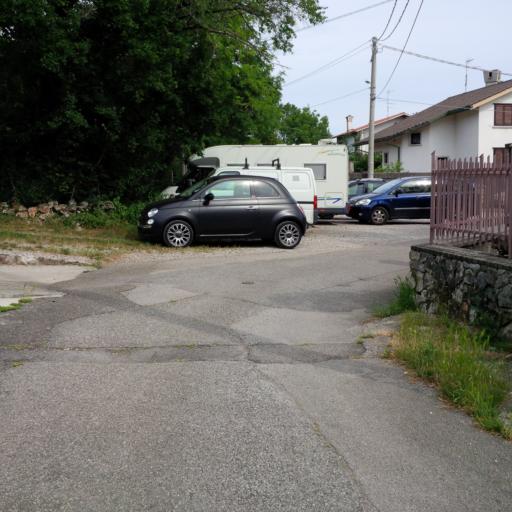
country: IT
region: Friuli Venezia Giulia
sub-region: Provincia di Trieste
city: Villa Opicina
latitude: 45.6873
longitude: 13.7998
